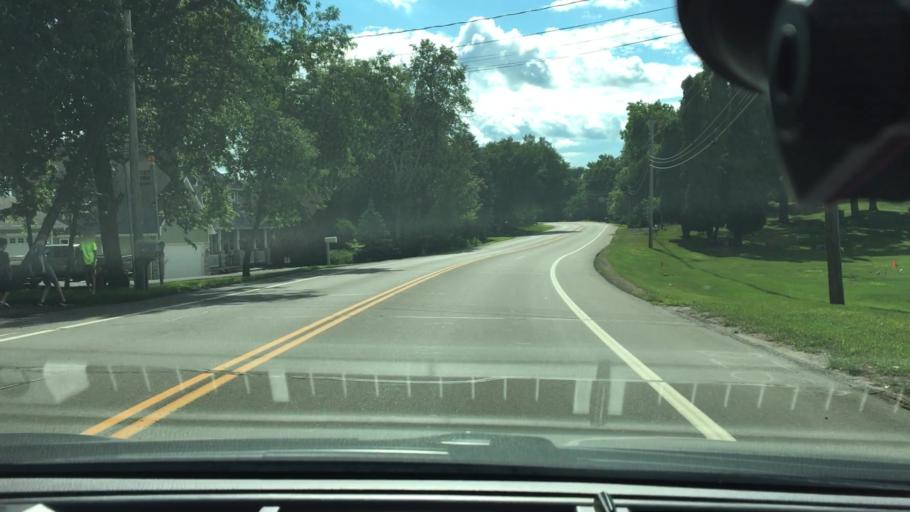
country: US
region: Minnesota
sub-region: Hennepin County
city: Mound
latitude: 44.9248
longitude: -93.6857
